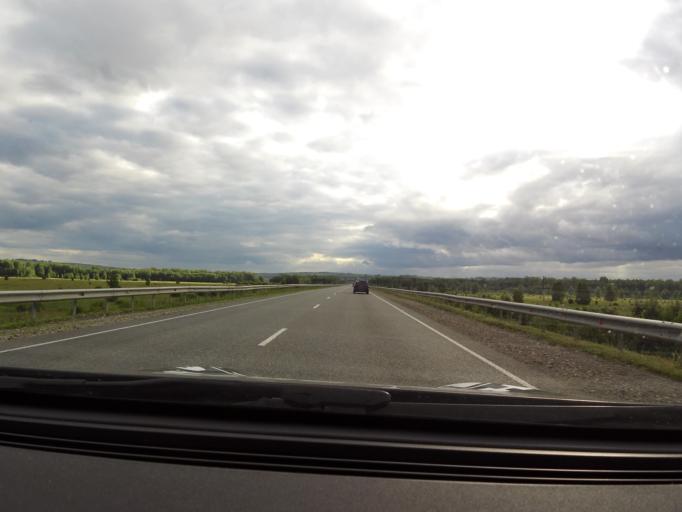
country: RU
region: Tatarstan
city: Sviyazhsk
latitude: 55.7123
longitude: 48.6967
